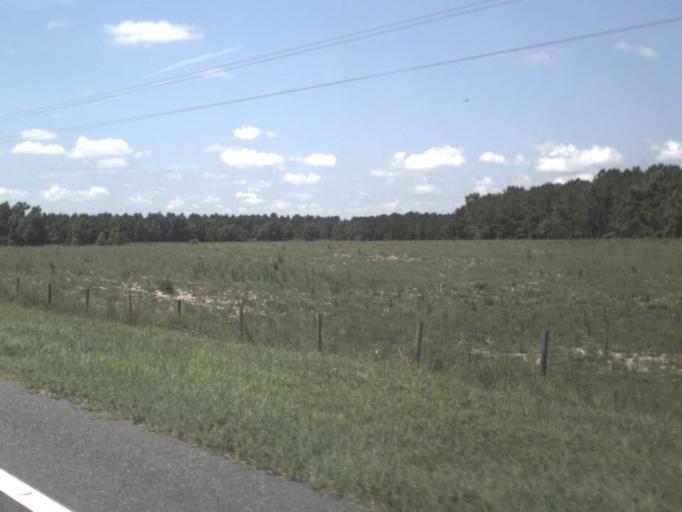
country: US
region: Florida
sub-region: Levy County
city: Williston
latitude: 29.4697
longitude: -82.4149
